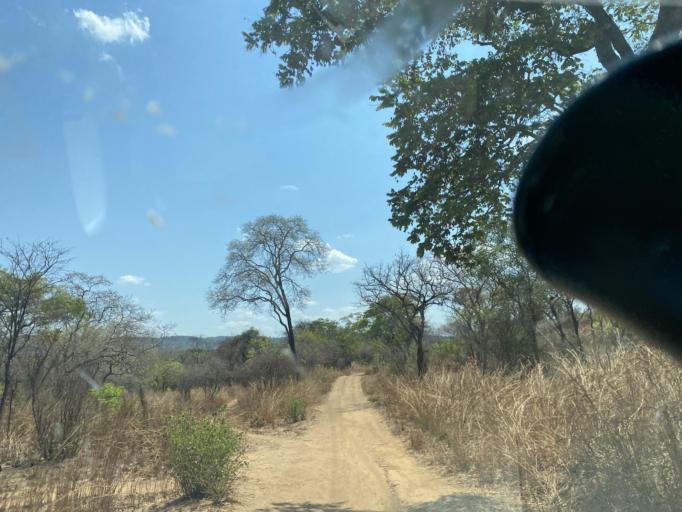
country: ZM
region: Lusaka
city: Chongwe
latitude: -15.0881
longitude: 29.4939
